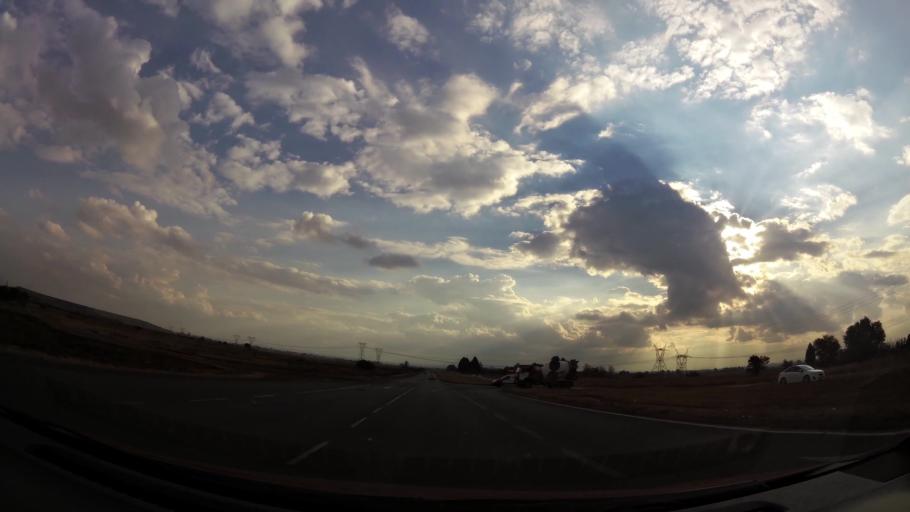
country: ZA
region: Gauteng
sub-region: Sedibeng District Municipality
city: Vanderbijlpark
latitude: -26.6189
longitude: 27.8328
